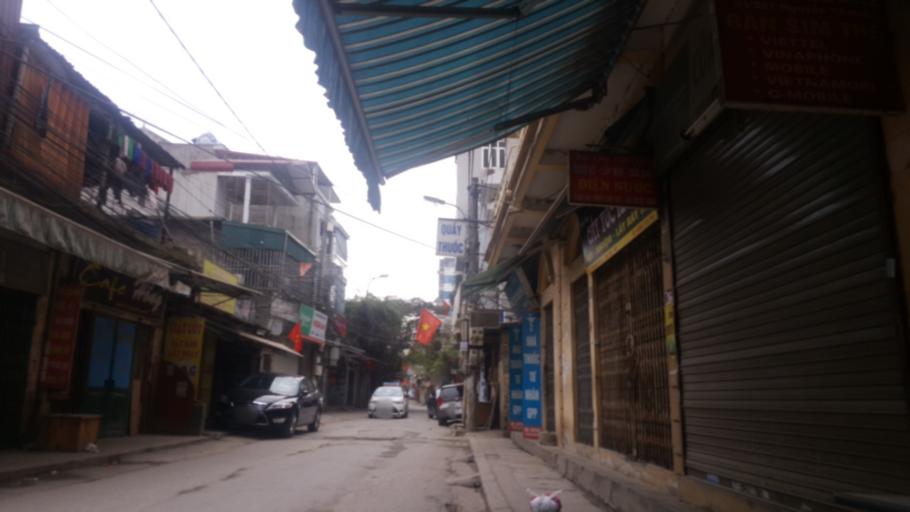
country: VN
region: Ha Noi
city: Cau Giay
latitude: 21.0277
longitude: 105.7963
